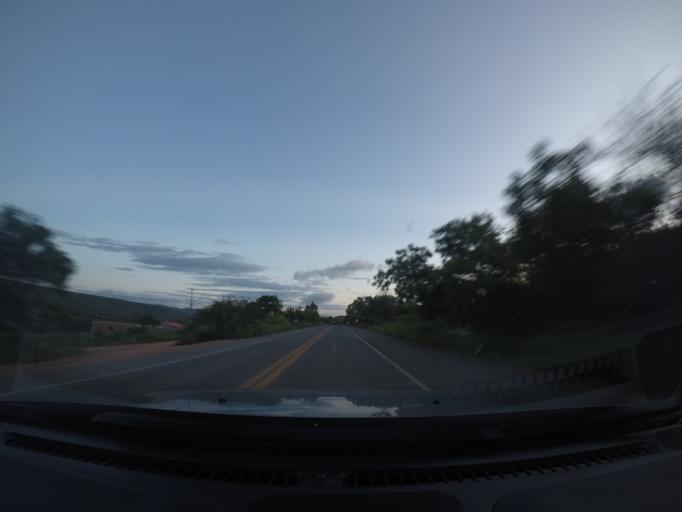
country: BR
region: Bahia
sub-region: Seabra
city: Seabra
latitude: -12.4536
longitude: -41.7502
